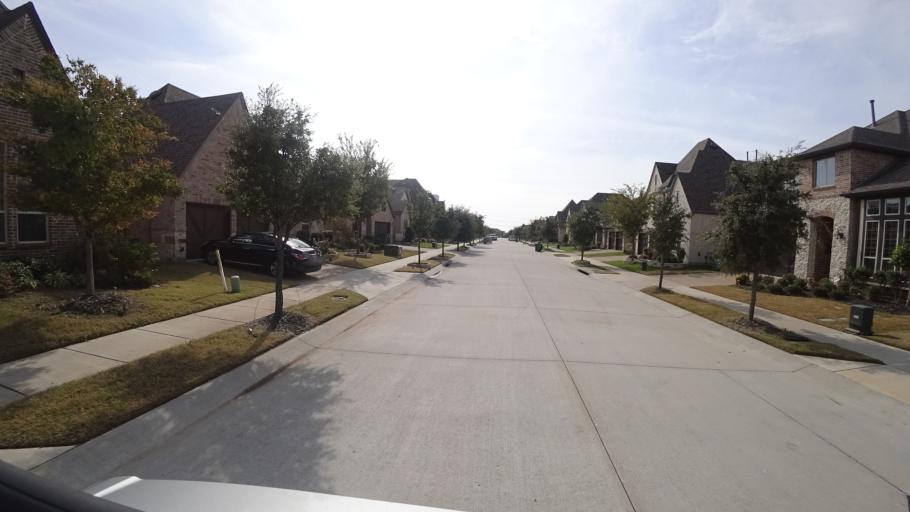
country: US
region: Texas
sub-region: Denton County
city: The Colony
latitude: 33.0654
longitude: -96.8771
